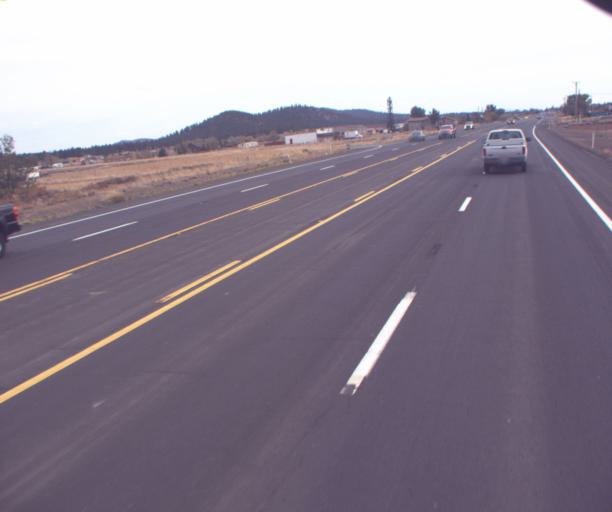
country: US
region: Arizona
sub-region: Coconino County
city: Flagstaff
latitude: 35.3148
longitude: -111.5428
